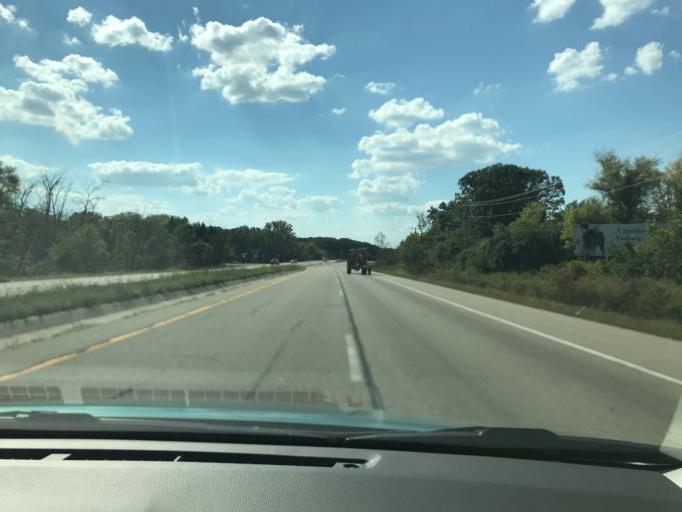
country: US
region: Wisconsin
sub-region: Walworth County
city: Como
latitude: 42.5837
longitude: -88.4959
